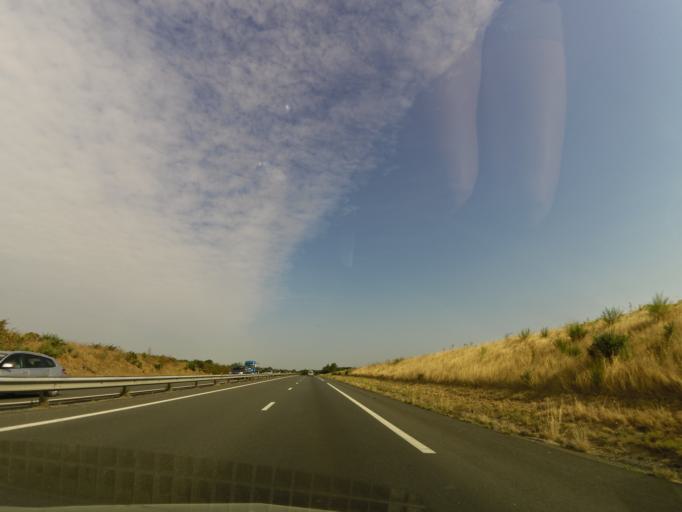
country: FR
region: Pays de la Loire
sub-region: Departement de la Loire-Atlantique
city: La Planche
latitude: 47.0403
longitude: -1.4099
